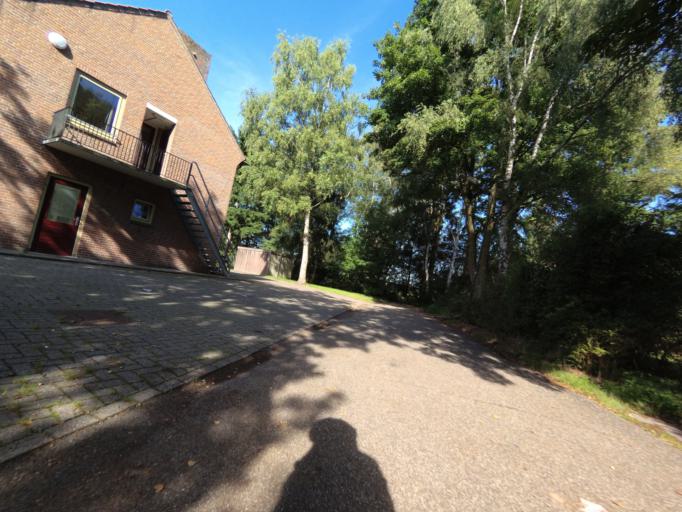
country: NL
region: Utrecht
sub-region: Gemeente Utrechtse Heuvelrug
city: Maarsbergen
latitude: 52.0410
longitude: 5.4227
